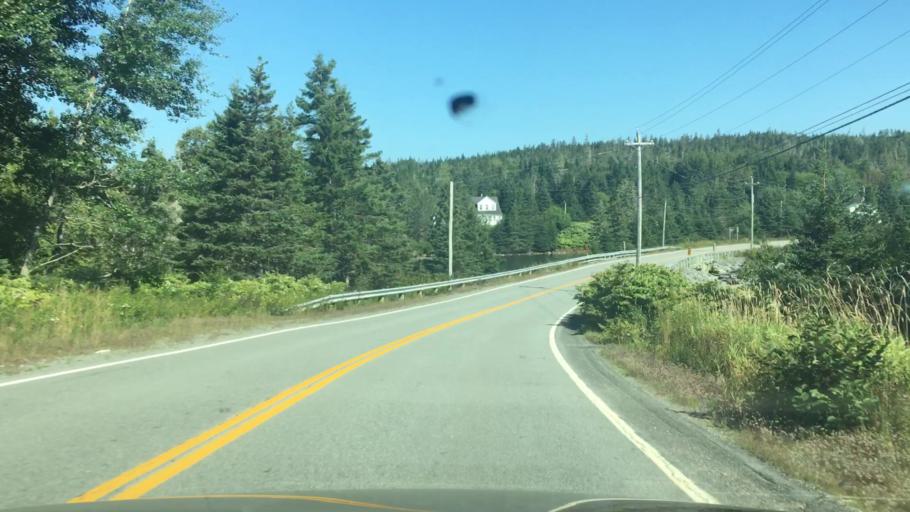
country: CA
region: Nova Scotia
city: New Glasgow
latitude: 44.8211
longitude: -62.6347
